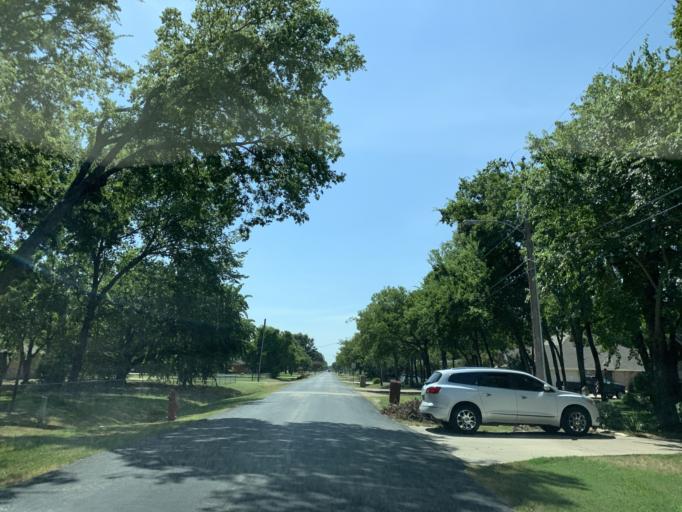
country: US
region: Texas
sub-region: Dallas County
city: Cedar Hill
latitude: 32.6503
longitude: -97.0152
